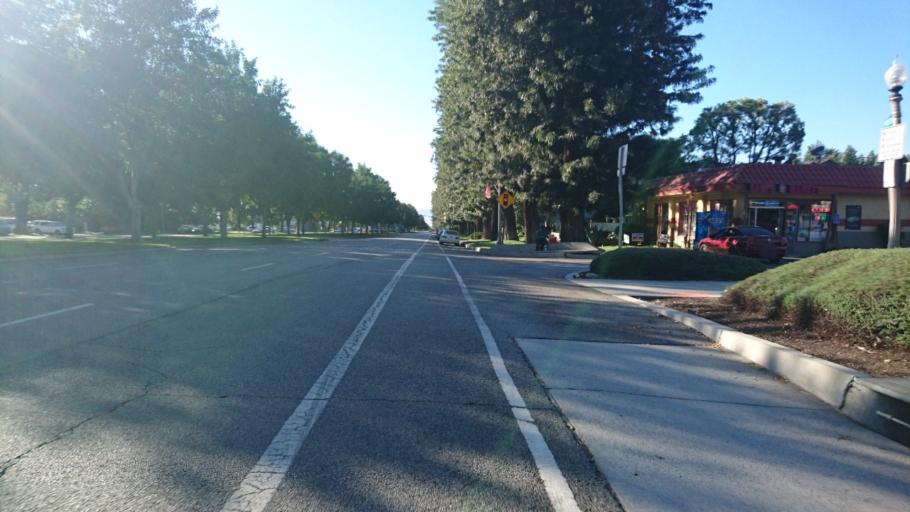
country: US
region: California
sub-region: San Bernardino County
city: Upland
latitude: 34.0980
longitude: -117.6514
